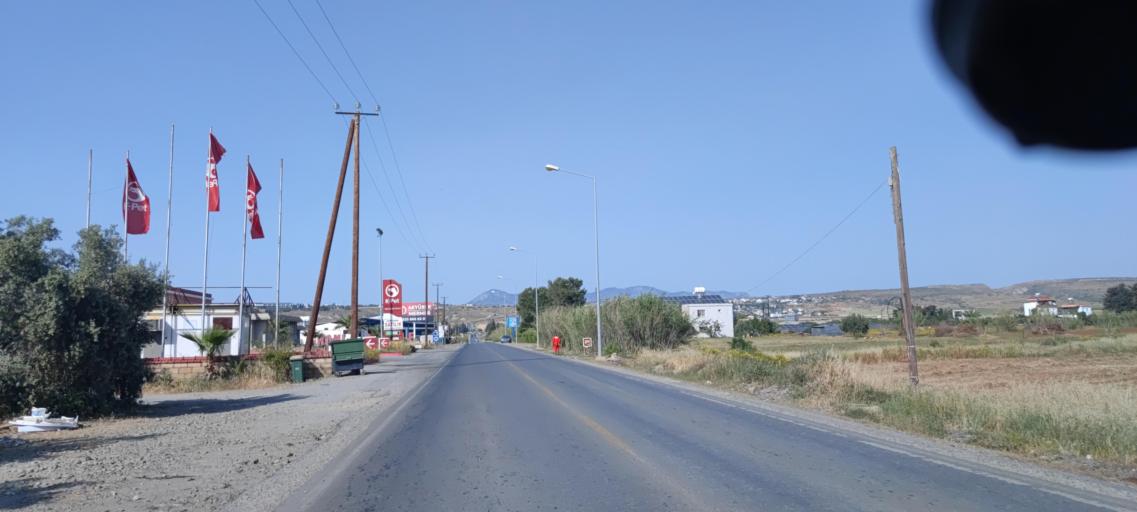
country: CY
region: Lefkosia
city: Morfou
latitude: 35.2333
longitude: 33.0183
